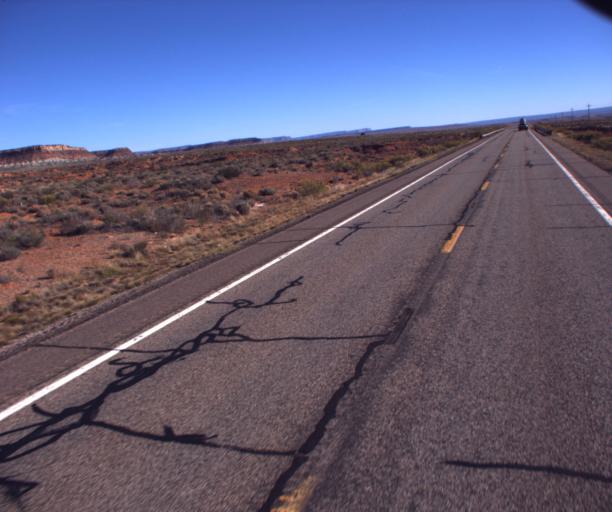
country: US
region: Arizona
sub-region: Coconino County
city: Fredonia
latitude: 36.8746
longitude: -112.6655
